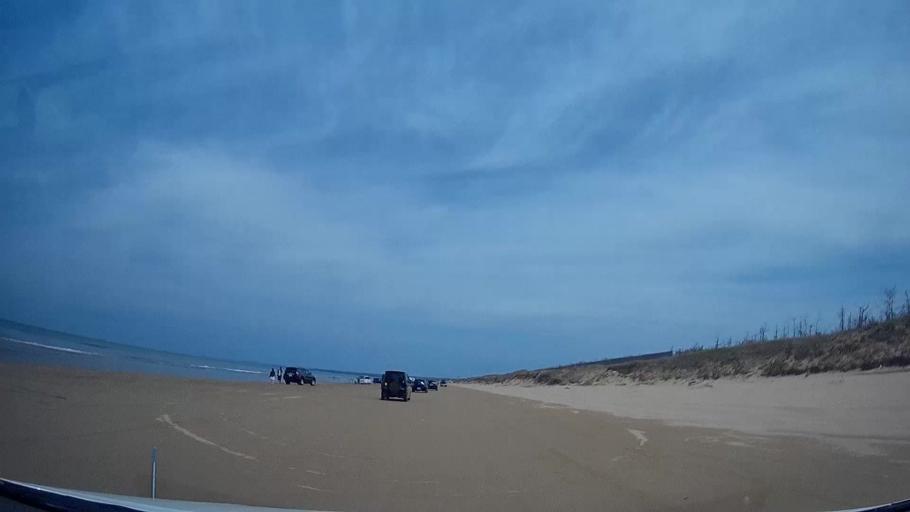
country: JP
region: Ishikawa
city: Hakui
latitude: 36.8448
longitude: 136.7513
